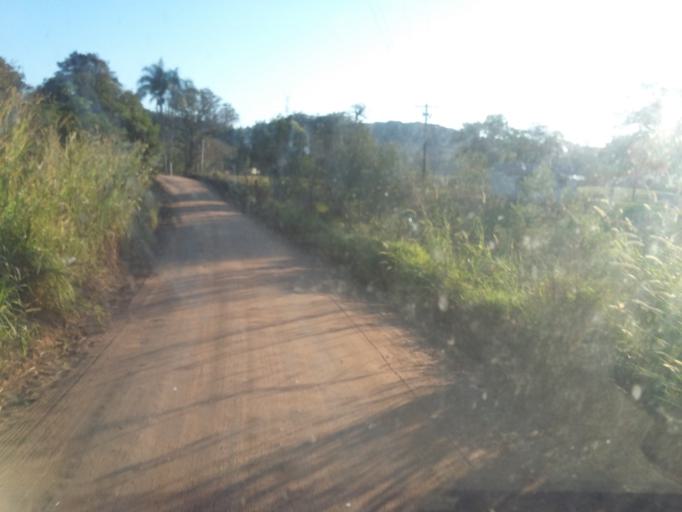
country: BR
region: Rio Grande do Sul
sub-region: Camaqua
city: Camaqua
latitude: -30.7251
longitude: -51.7723
